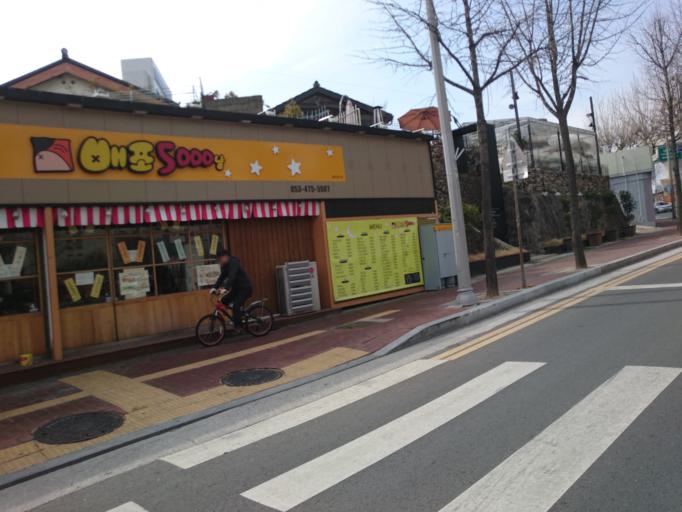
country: KR
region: Daegu
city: Daegu
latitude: 35.8556
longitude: 128.5980
